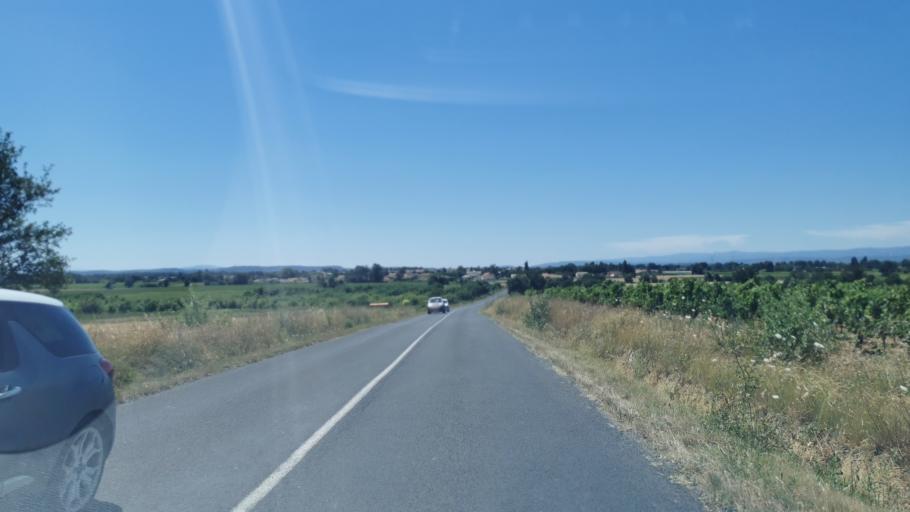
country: FR
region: Languedoc-Roussillon
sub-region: Departement de l'Aude
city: Coursan
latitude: 43.2326
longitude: 3.0832
